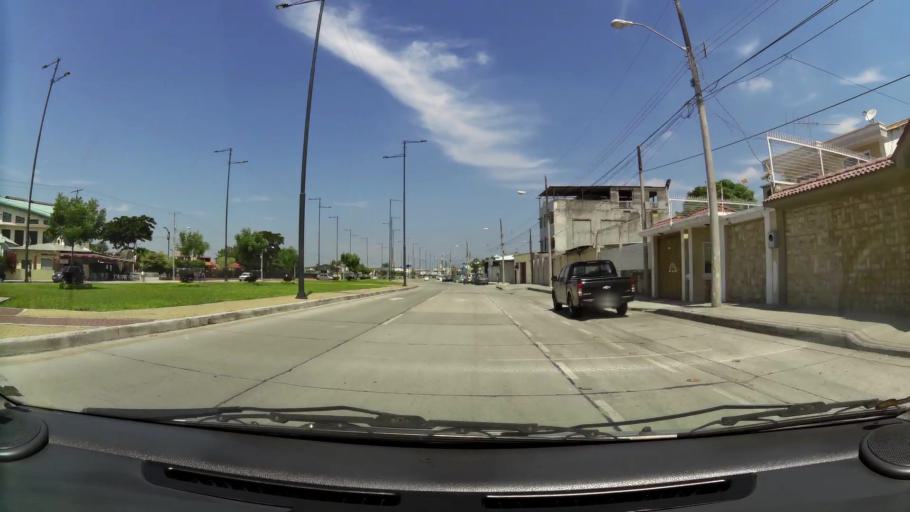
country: EC
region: Guayas
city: Eloy Alfaro
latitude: -2.1083
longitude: -79.8991
